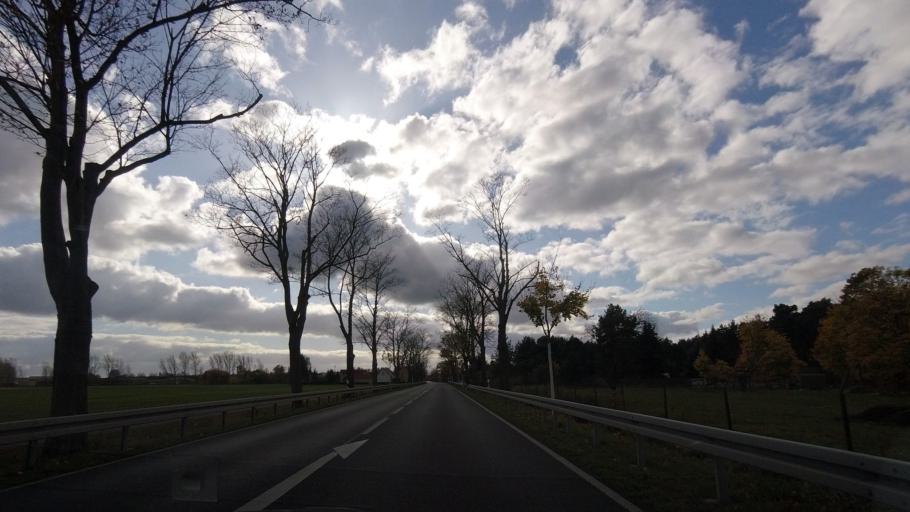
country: DE
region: Brandenburg
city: Beelitz
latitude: 52.1657
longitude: 12.9265
